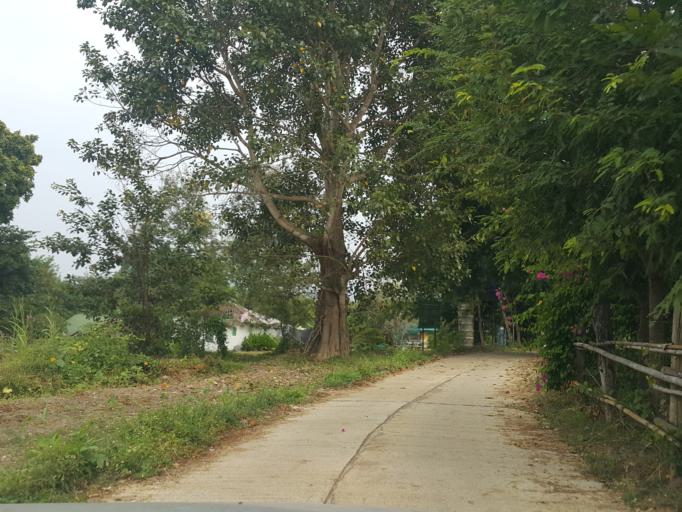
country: TH
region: Mae Hong Son
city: Wiang Nuea
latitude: 19.3726
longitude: 98.4467
